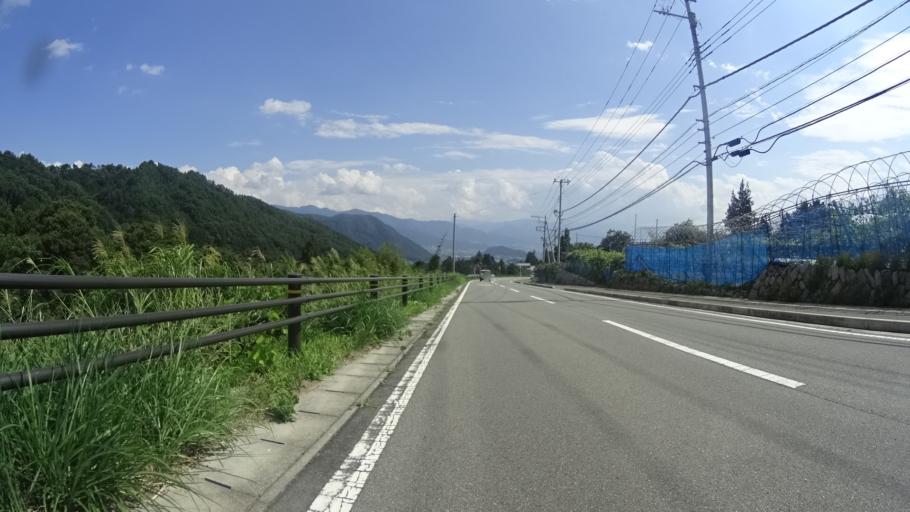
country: JP
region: Yamanashi
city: Enzan
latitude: 35.7617
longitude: 138.7057
